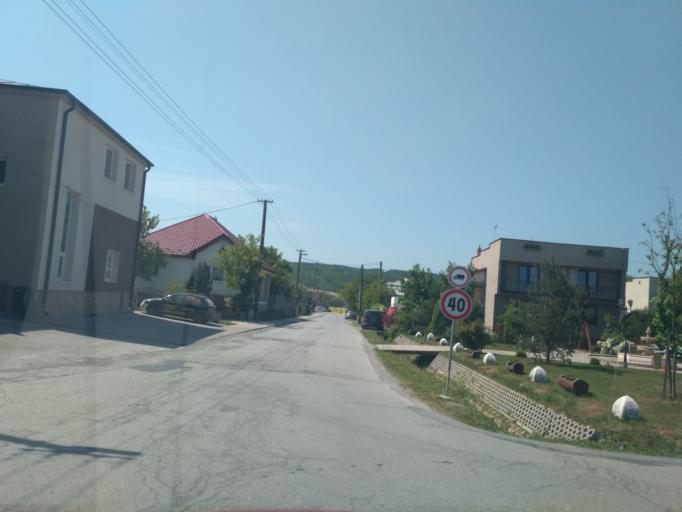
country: SK
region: Kosicky
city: Kosice
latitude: 48.7819
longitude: 21.3258
